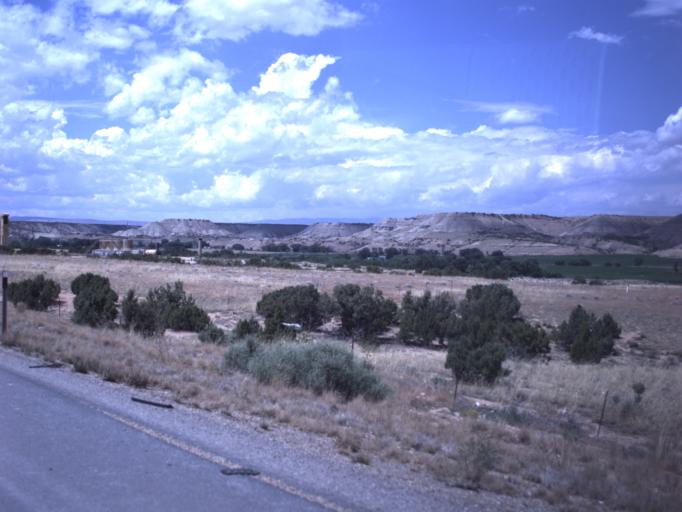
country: US
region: Utah
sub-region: Duchesne County
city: Duchesne
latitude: 40.1714
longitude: -110.3312
